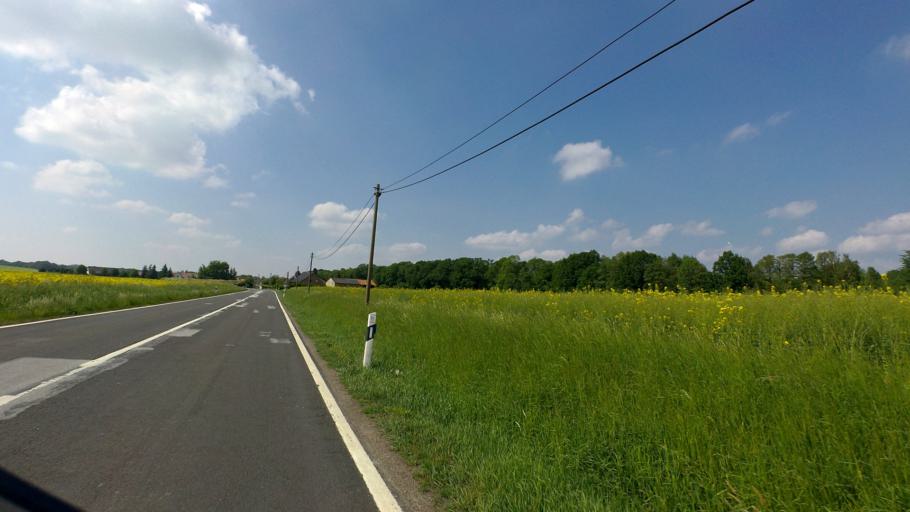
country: DE
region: Saxony
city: Hochkirch
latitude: 51.1905
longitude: 14.6067
